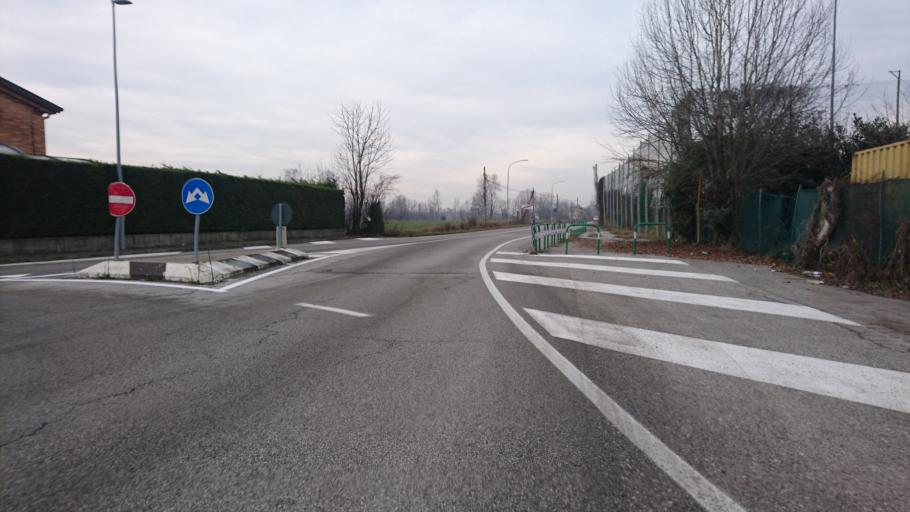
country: IT
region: Veneto
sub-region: Provincia di Padova
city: Taggi
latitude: 45.4594
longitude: 11.8152
